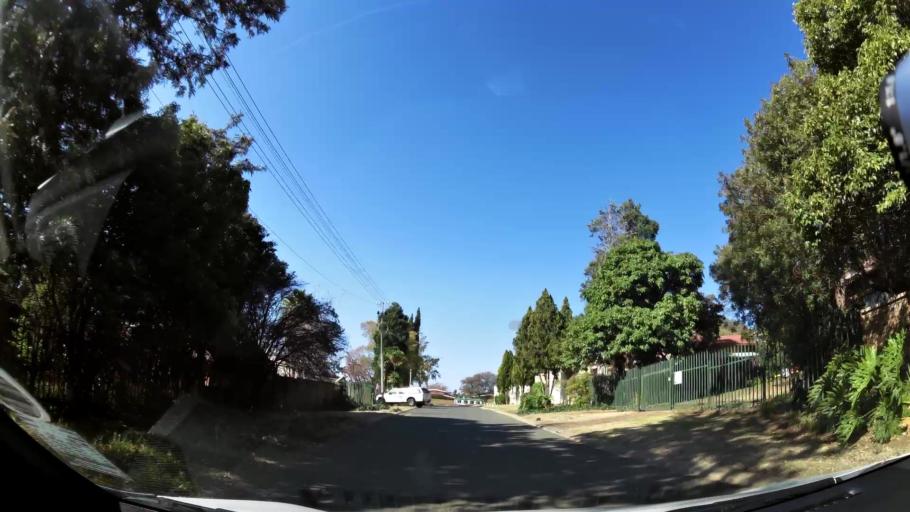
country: ZA
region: Gauteng
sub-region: City of Johannesburg Metropolitan Municipality
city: Johannesburg
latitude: -26.2783
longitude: 28.0190
